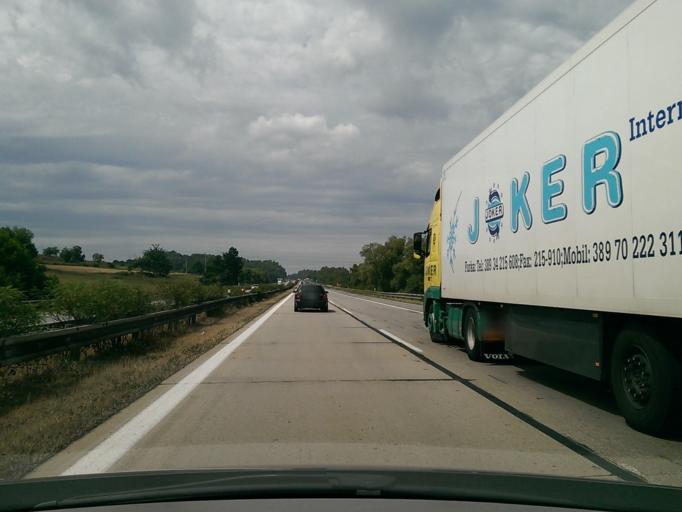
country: CZ
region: Vysocina
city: Merin
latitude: 49.4017
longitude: 15.8541
